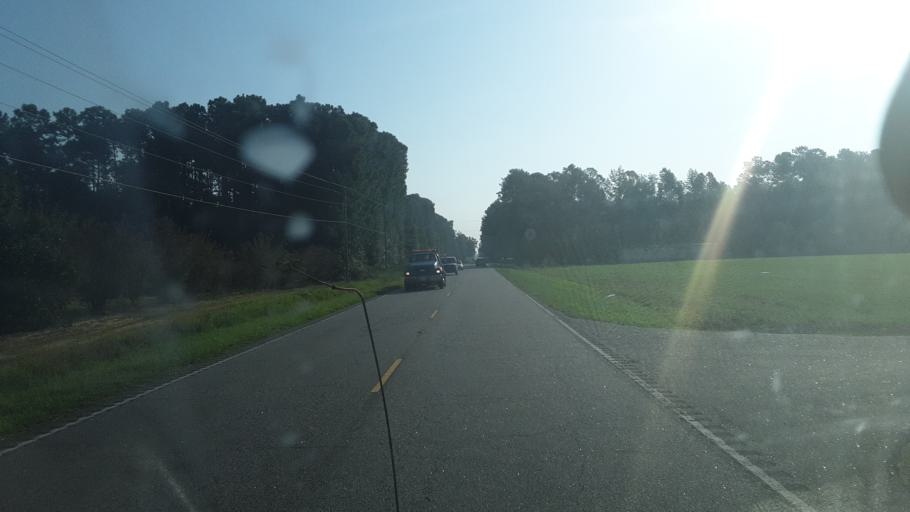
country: US
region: South Carolina
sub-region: Horry County
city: Forestbrook
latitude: 33.8388
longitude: -78.8713
